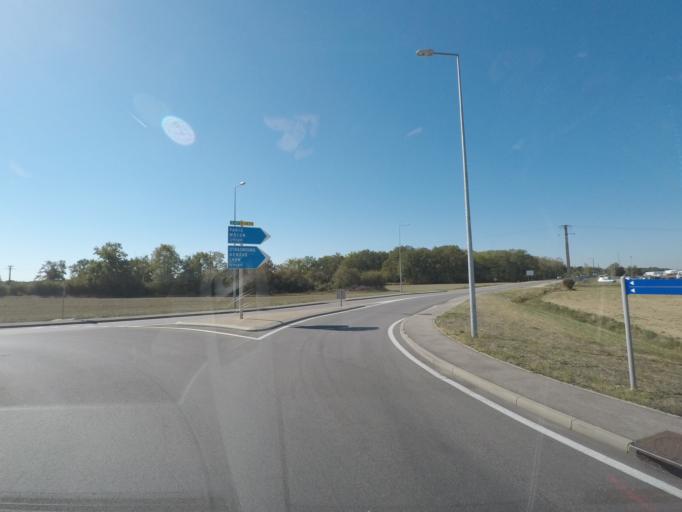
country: FR
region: Rhone-Alpes
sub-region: Departement de l'Ain
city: Attignat
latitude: 46.2596
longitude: 5.1765
